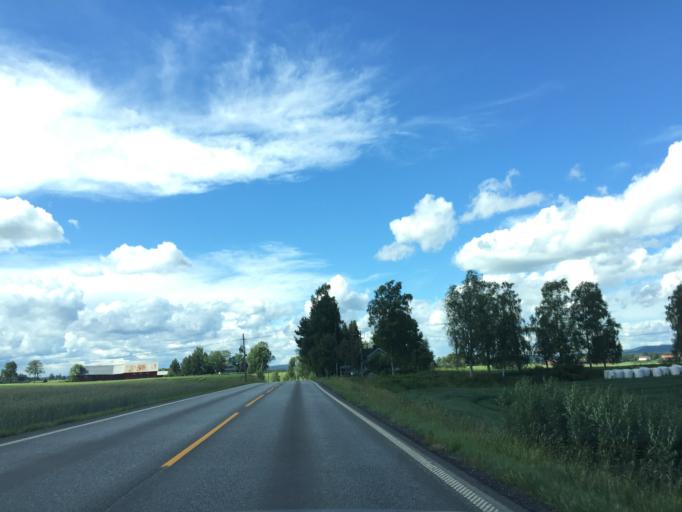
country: NO
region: Akershus
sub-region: Nes
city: Arnes
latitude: 60.1394
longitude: 11.4292
